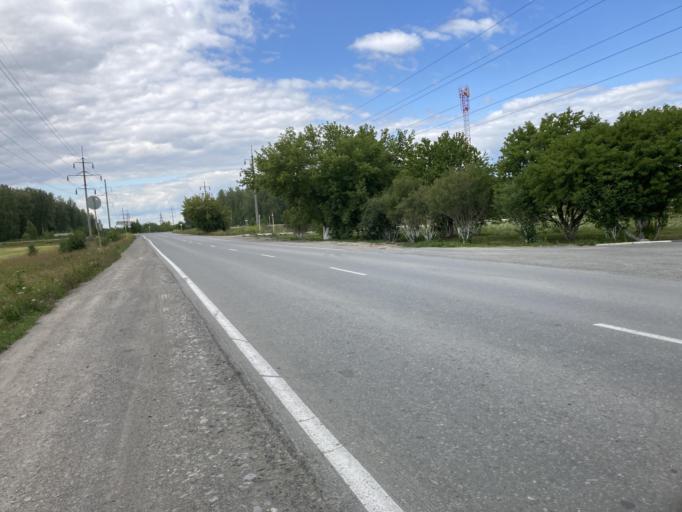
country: RU
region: Sverdlovsk
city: Bogdanovich
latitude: 56.8060
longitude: 62.0346
